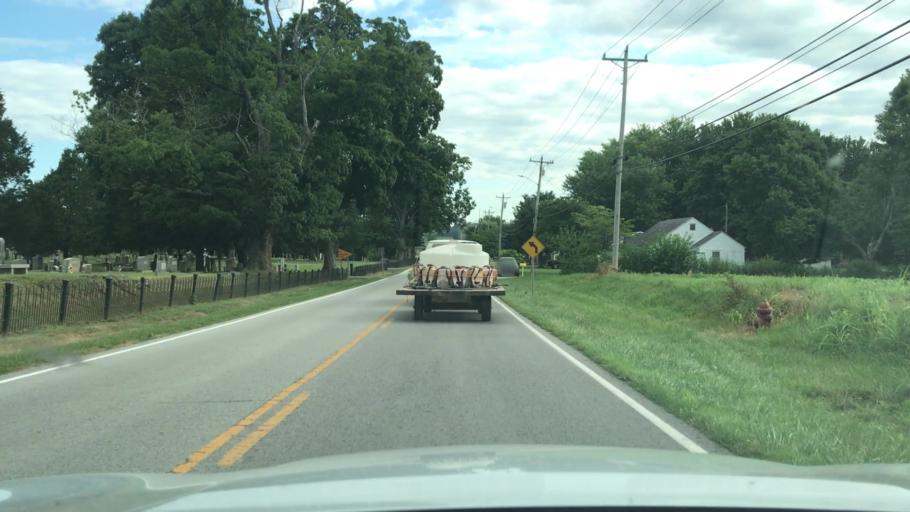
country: US
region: Kentucky
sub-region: Todd County
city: Elkton
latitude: 36.8173
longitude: -87.1519
